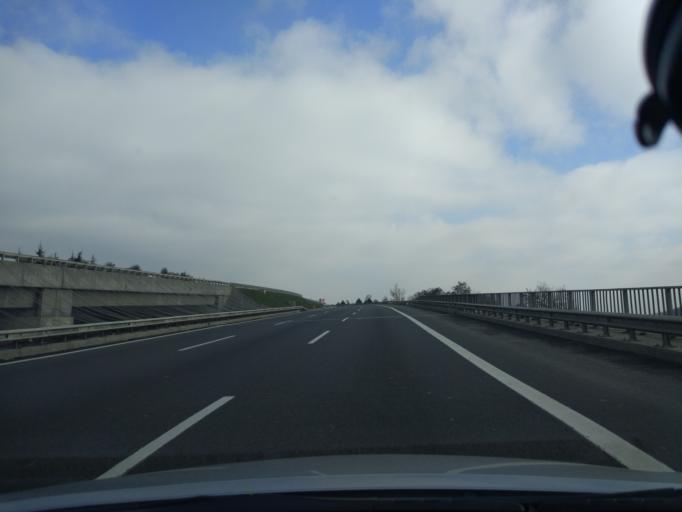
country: TR
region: Bolu
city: Bolu
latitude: 40.7251
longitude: 31.5044
